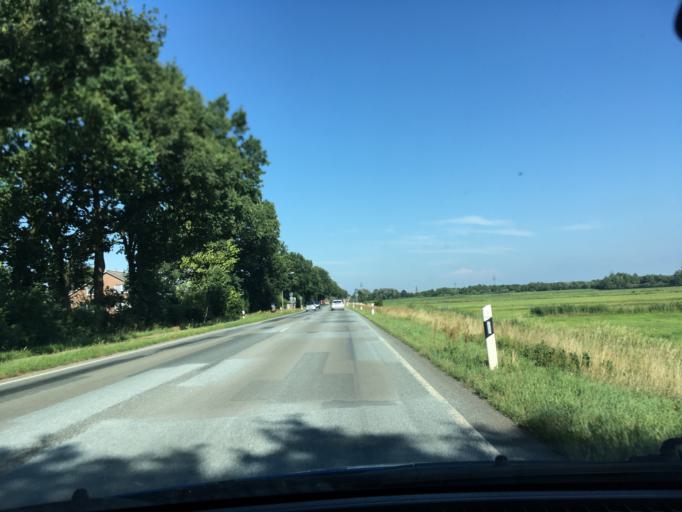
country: DE
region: Lower Saxony
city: Winsen
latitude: 53.3669
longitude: 10.1673
